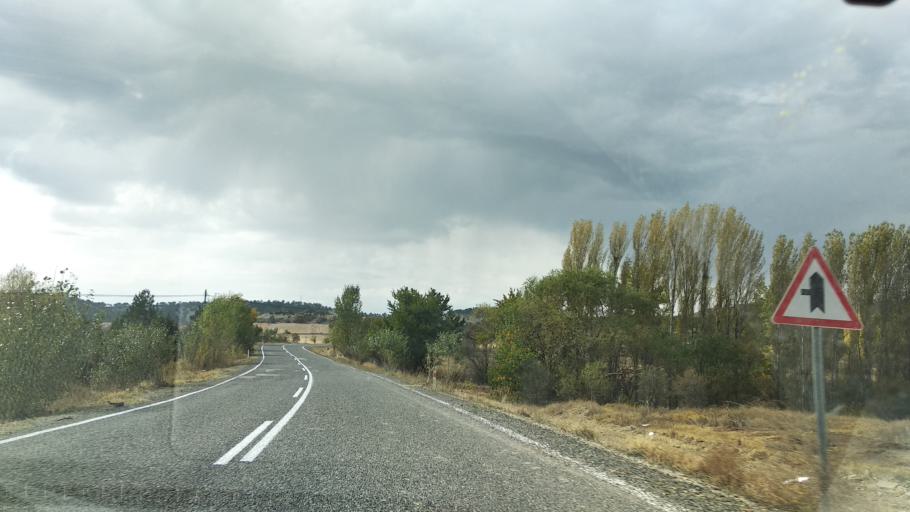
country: TR
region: Bolu
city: Seben
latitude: 40.3644
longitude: 31.4970
